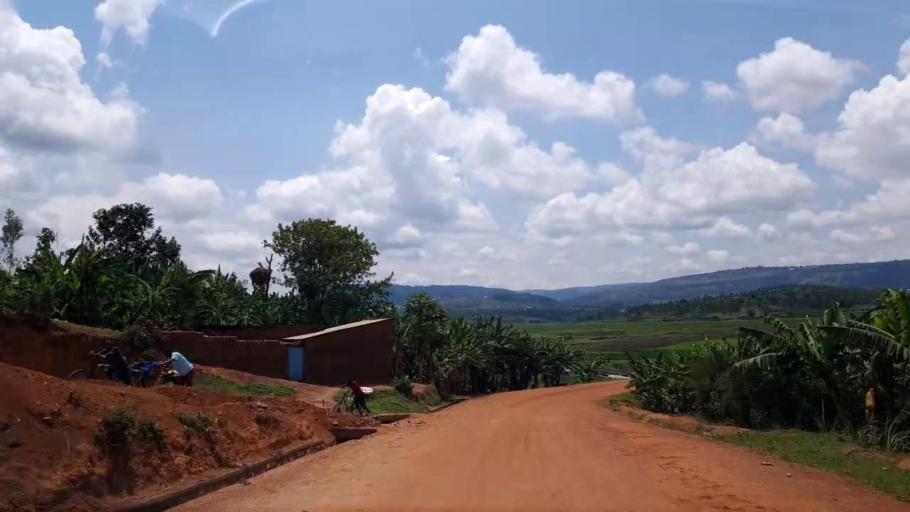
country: RW
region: Northern Province
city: Byumba
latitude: -1.5703
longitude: 30.2945
